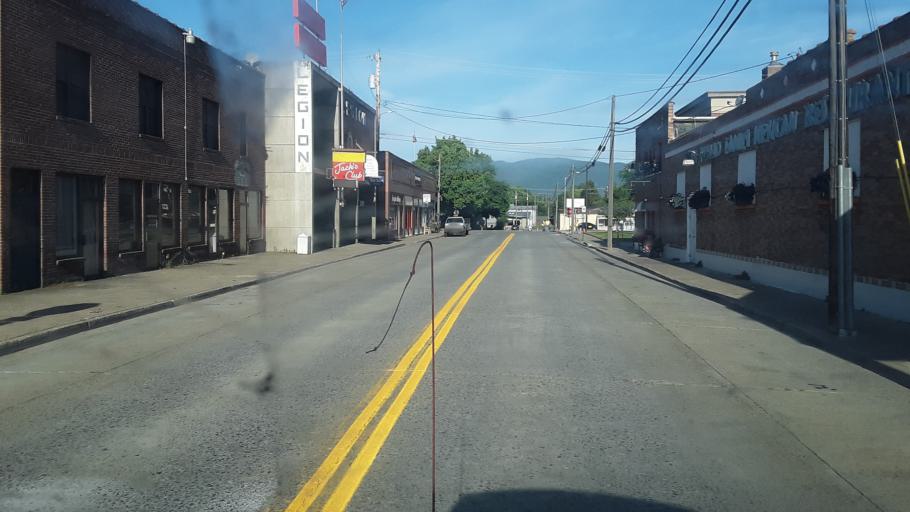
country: US
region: Idaho
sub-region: Boundary County
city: Bonners Ferry
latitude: 48.6964
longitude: -116.3118
